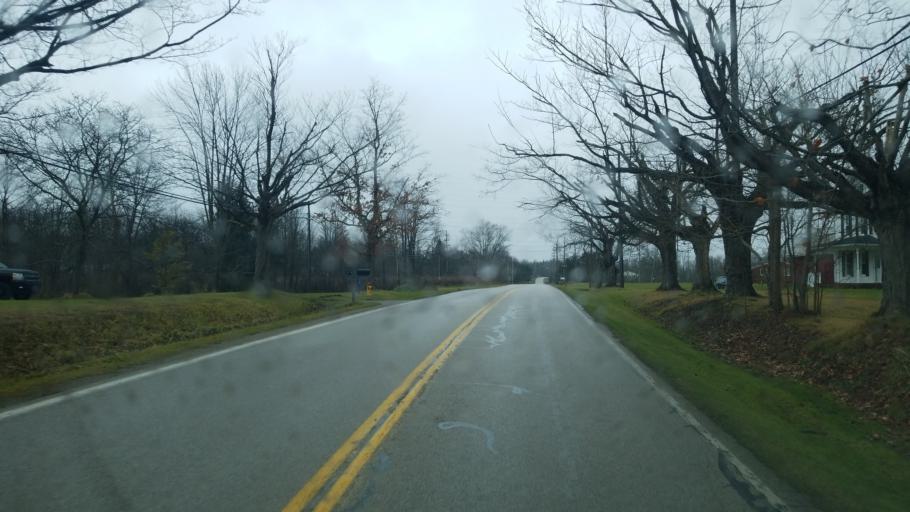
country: US
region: Ohio
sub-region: Ashtabula County
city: Ashtabula
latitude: 41.8255
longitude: -80.8054
